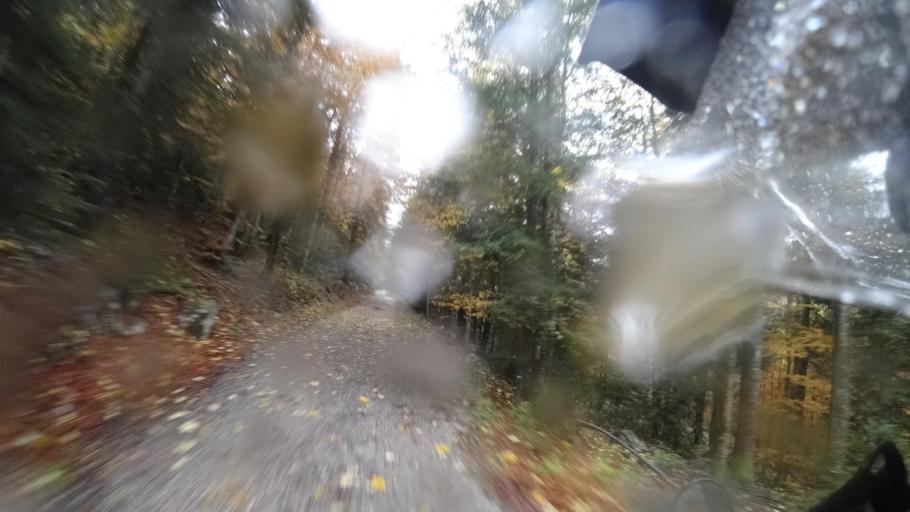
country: HR
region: Primorsko-Goranska
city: Vrbovsko
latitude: 45.3018
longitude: 14.9901
